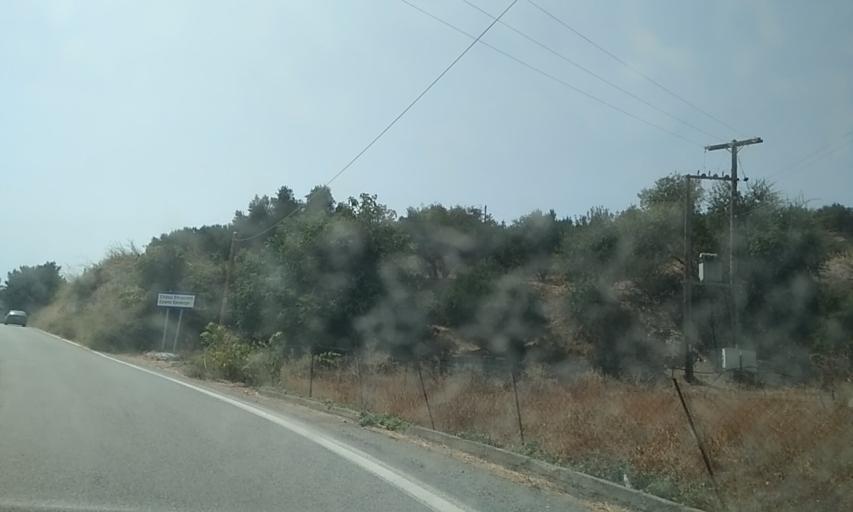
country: GR
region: Crete
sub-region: Nomos Lasithiou
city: Siteia
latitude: 35.1330
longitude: 26.0748
